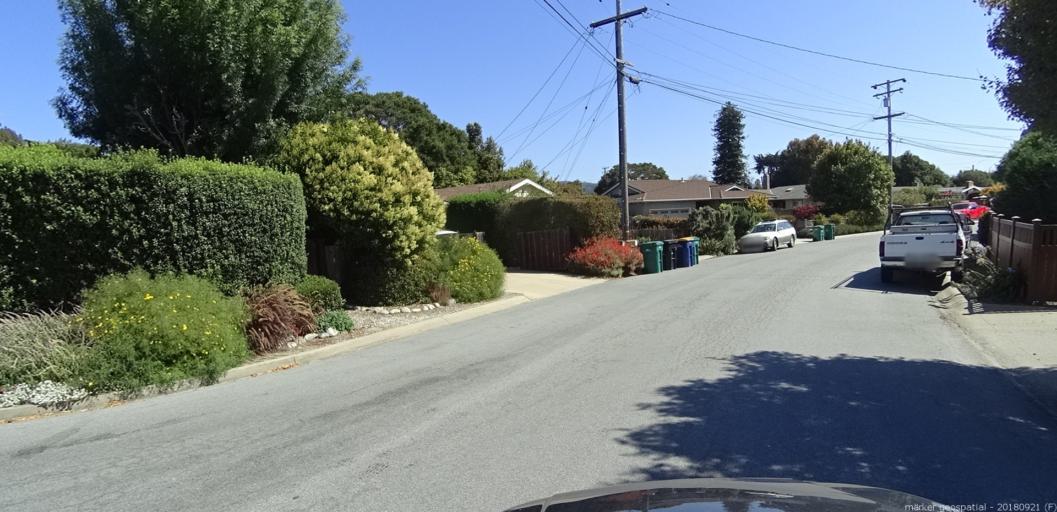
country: US
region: California
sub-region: Monterey County
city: Carmel-by-the-Sea
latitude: 36.5397
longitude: -121.9128
